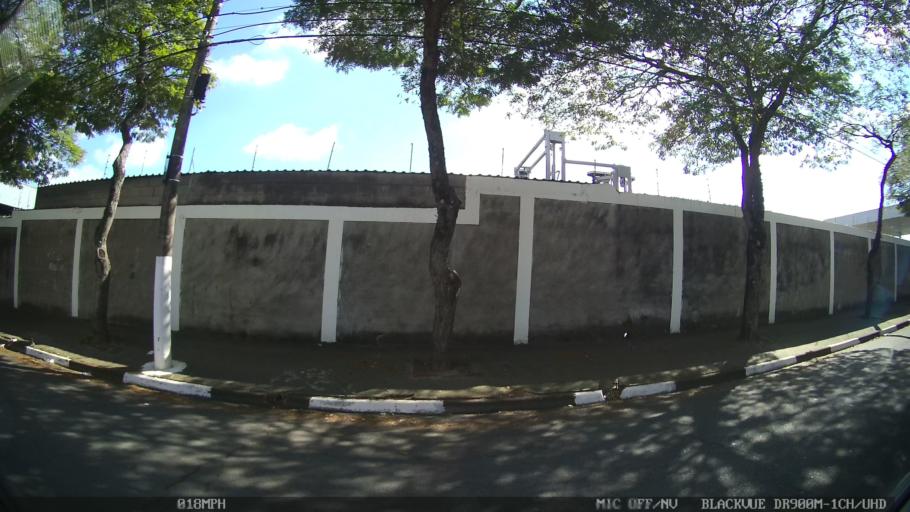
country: BR
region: Sao Paulo
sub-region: Hortolandia
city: Hortolandia
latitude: -22.8896
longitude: -47.1928
